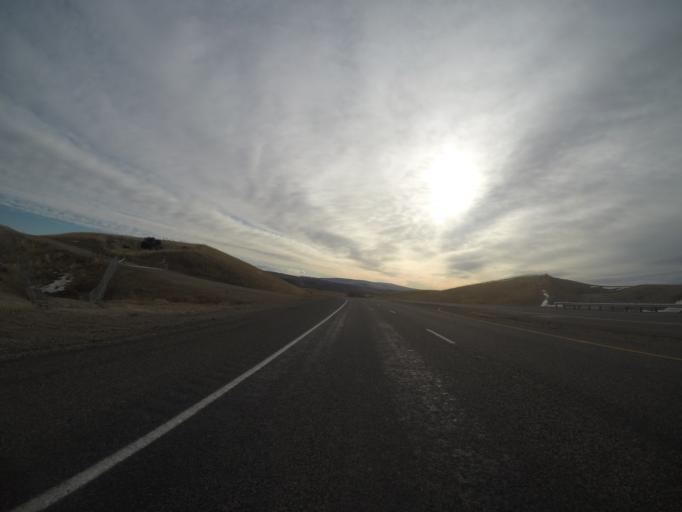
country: US
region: Montana
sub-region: Yellowstone County
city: Laurel
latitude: 45.5456
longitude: -108.8609
